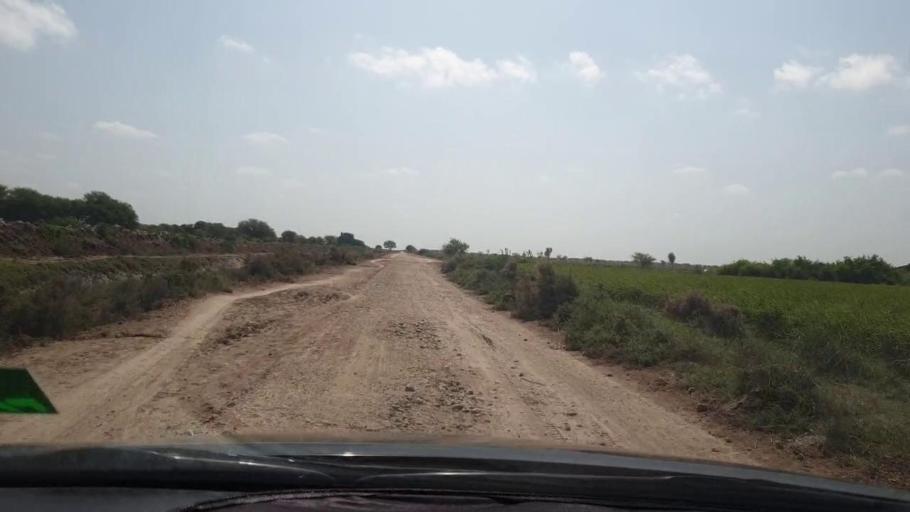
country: PK
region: Sindh
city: Tando Bago
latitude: 24.8427
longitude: 69.0419
